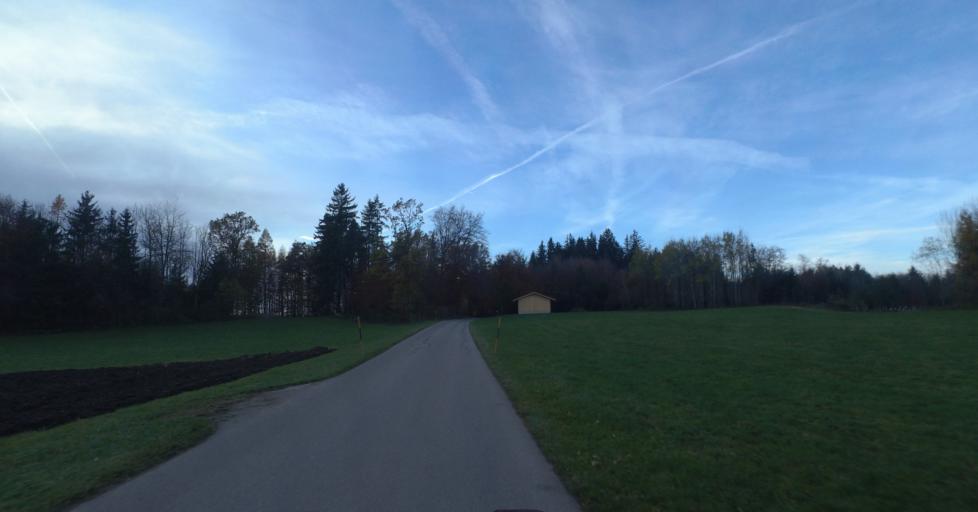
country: DE
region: Bavaria
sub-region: Upper Bavaria
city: Nussdorf
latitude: 47.8901
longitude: 12.6038
